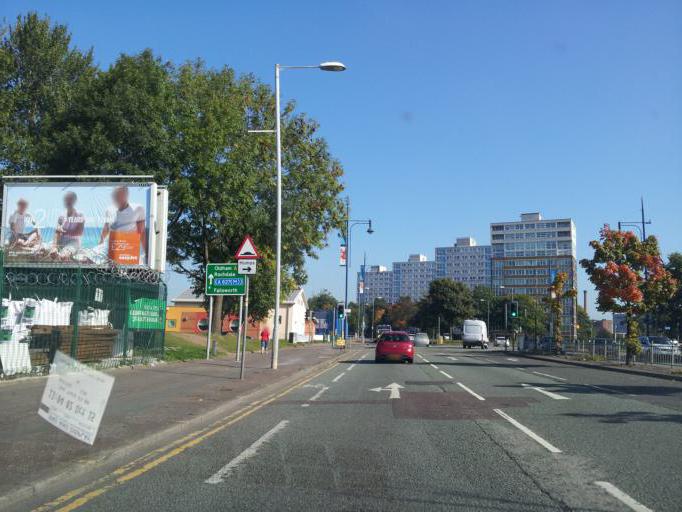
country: GB
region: England
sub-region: Manchester
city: Manchester
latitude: 53.4884
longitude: -2.2248
